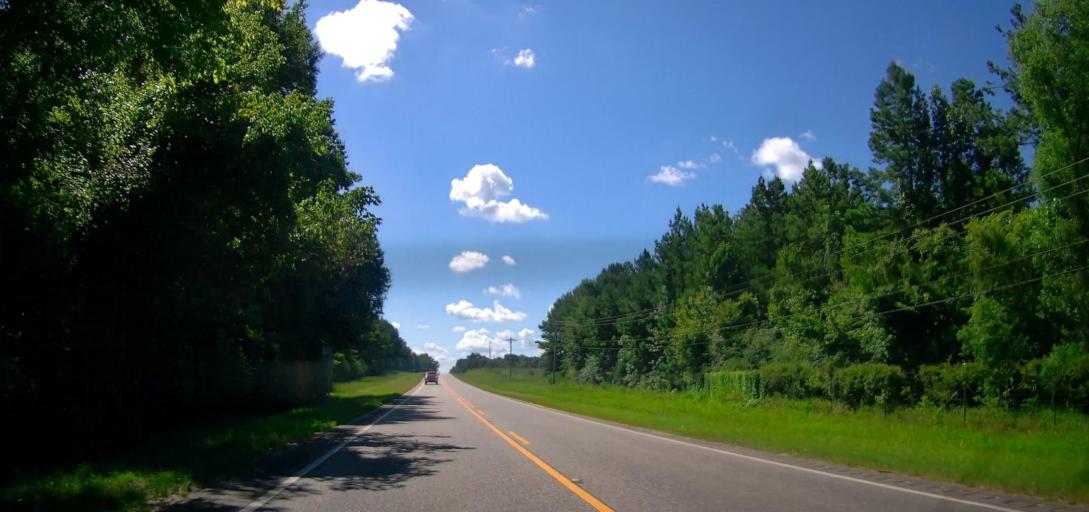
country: US
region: Alabama
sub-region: Macon County
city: Tuskegee
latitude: 32.3805
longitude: -85.7980
